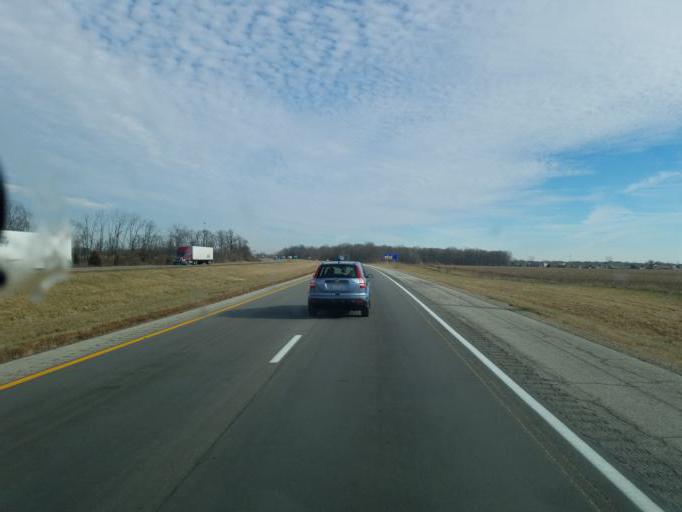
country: US
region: Ohio
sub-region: Montgomery County
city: Brookville
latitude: 39.8385
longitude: -84.4437
